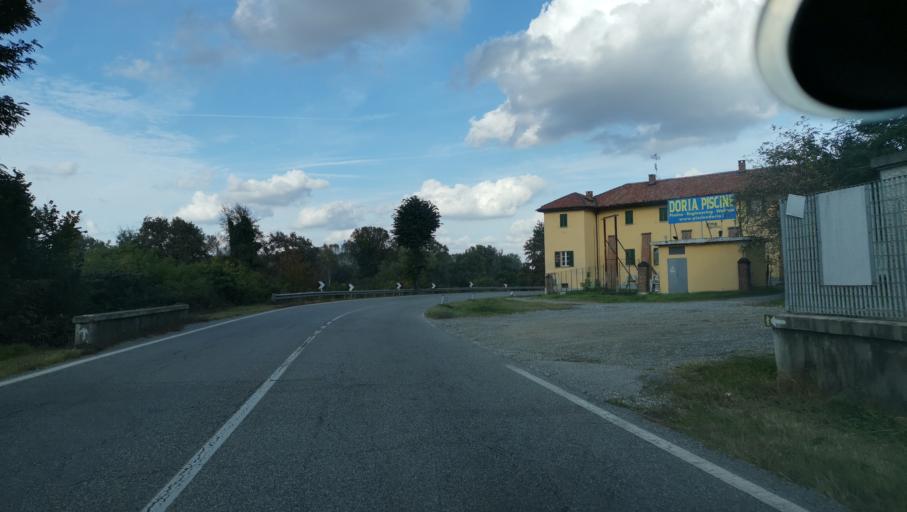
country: IT
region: Piedmont
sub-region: Provincia di Torino
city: Castagneto Po
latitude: 45.1753
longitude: 7.8793
